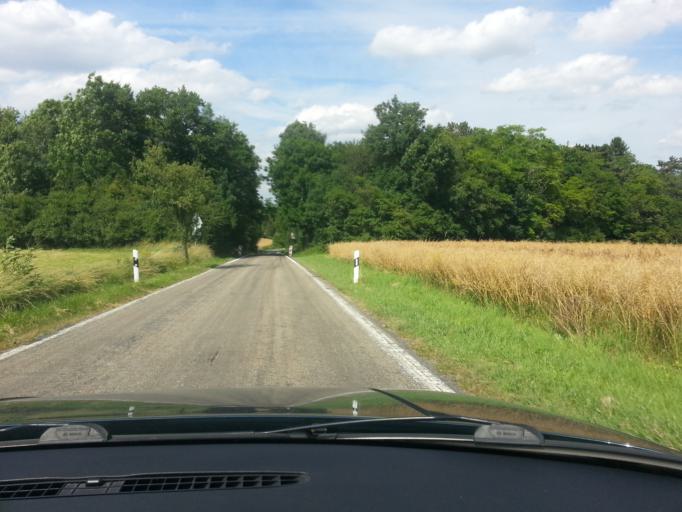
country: DE
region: Rheinland-Pfalz
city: Hornbach
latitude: 49.1751
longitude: 7.3355
